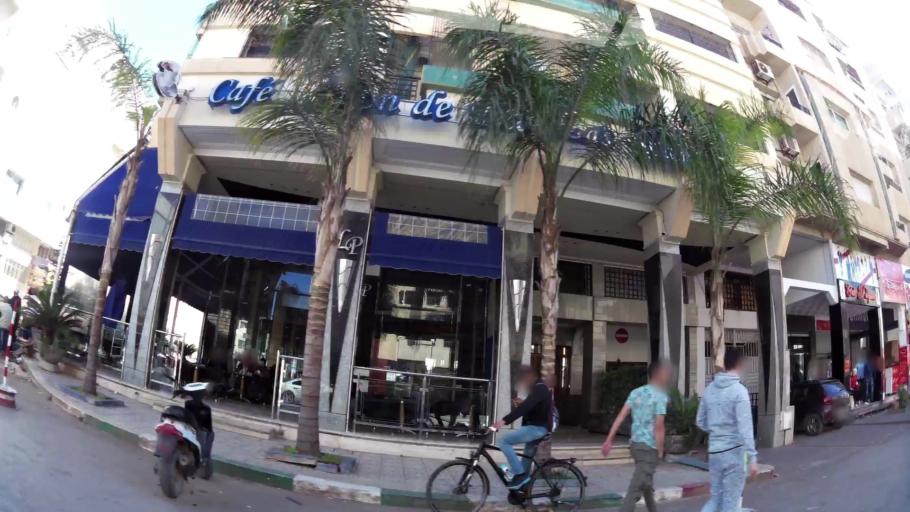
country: MA
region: Fes-Boulemane
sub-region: Fes
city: Fes
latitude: 34.0168
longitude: -4.9781
